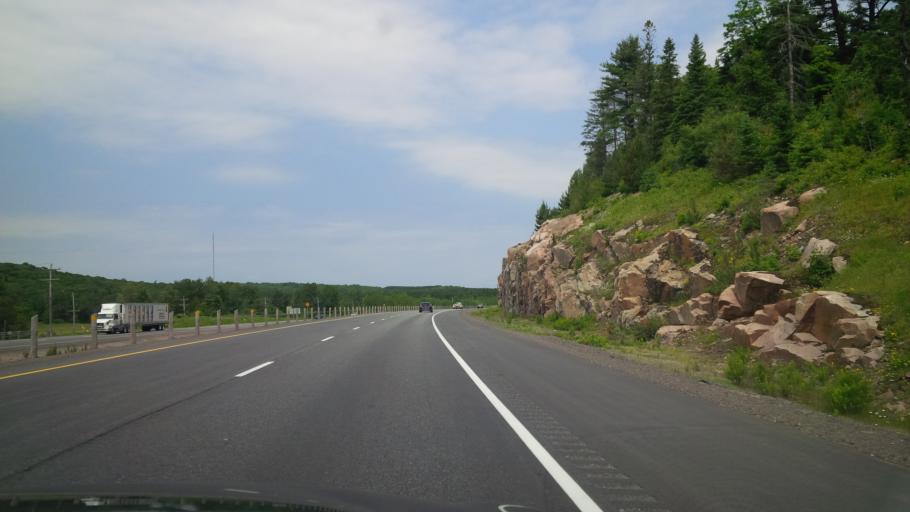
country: CA
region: Ontario
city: Huntsville
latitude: 45.3928
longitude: -79.2357
